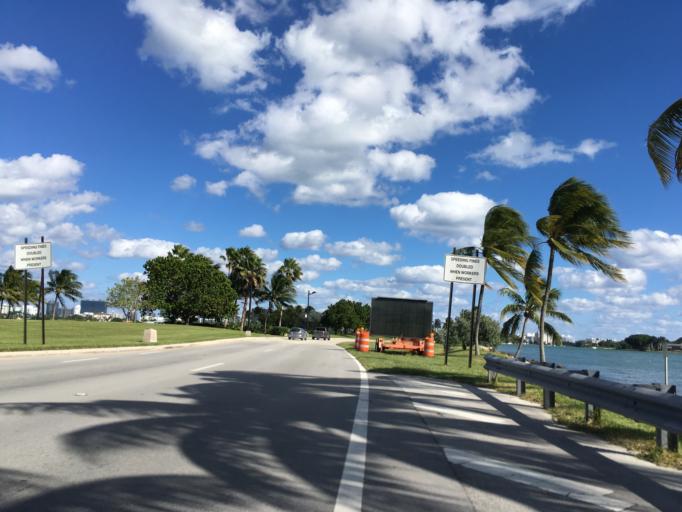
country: US
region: Florida
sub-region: Miami-Dade County
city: Bay Harbor Islands
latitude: 25.8881
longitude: -80.1474
